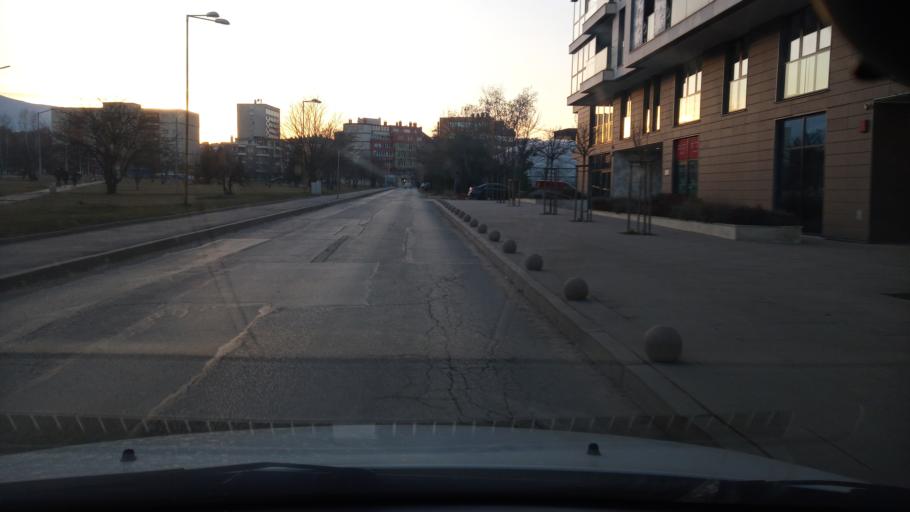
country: BG
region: Sofia-Capital
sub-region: Stolichna Obshtina
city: Sofia
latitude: 42.6567
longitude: 23.3525
